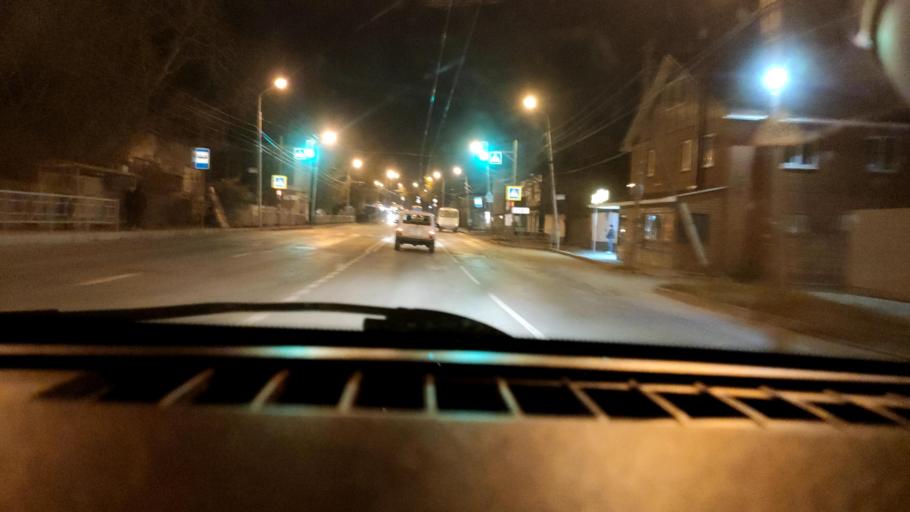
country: RU
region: Samara
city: Rozhdestveno
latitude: 53.1675
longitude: 50.0744
